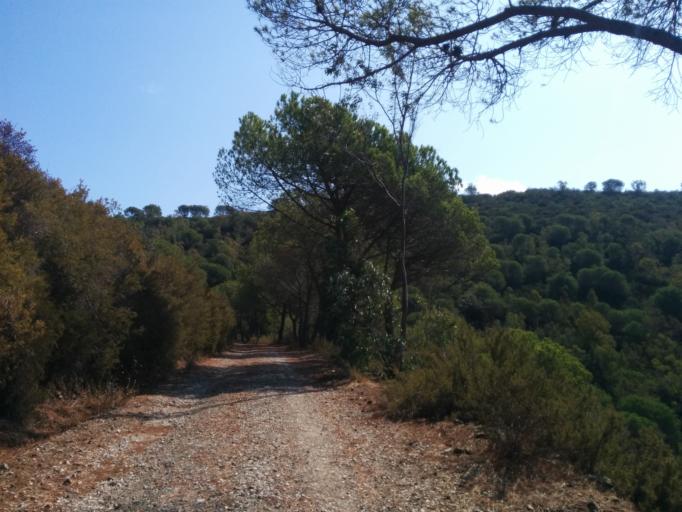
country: IT
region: Tuscany
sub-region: Provincia di Livorno
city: Capoliveri
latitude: 42.7429
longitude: 10.3163
